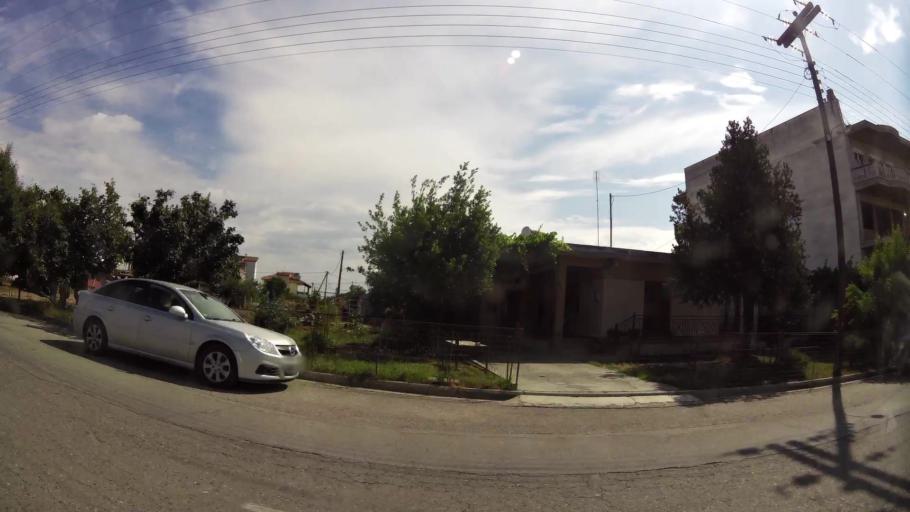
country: GR
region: Central Macedonia
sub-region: Nomos Pierias
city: Katerini
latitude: 40.2792
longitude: 22.4898
